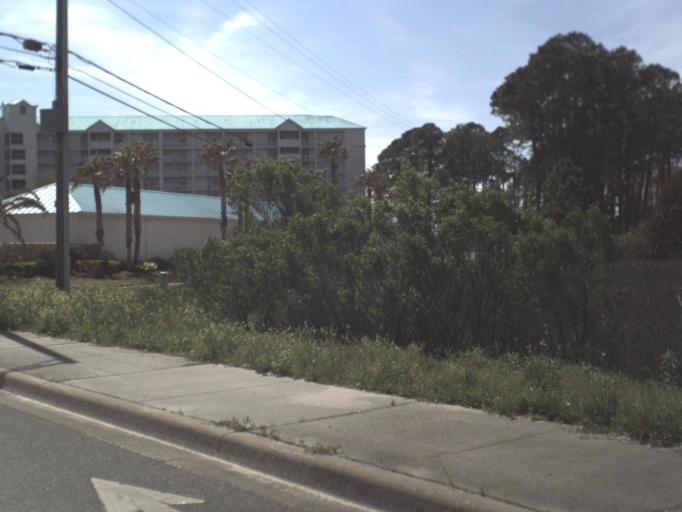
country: US
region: Florida
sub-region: Bay County
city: Lynn Haven
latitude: 30.2663
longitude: -85.6452
